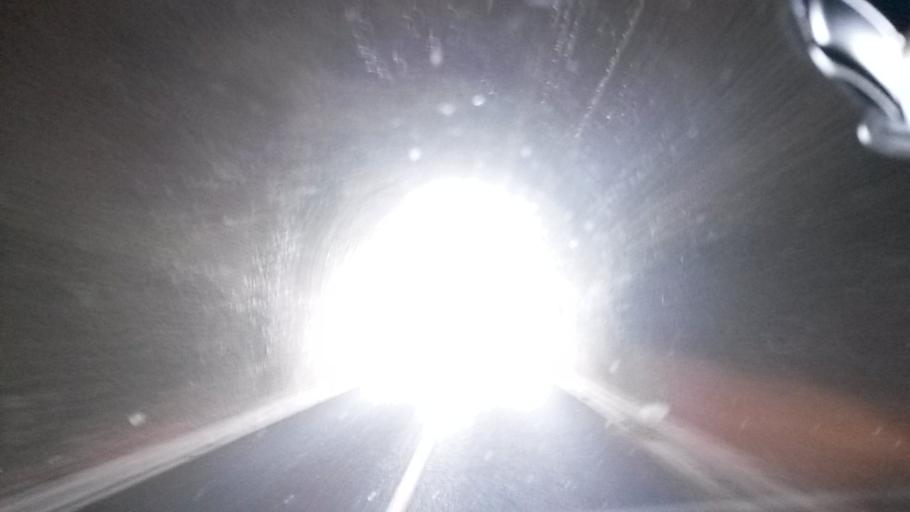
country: FR
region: Haute-Normandie
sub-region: Departement de l'Eure
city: Charleval
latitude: 49.3481
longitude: 1.4545
